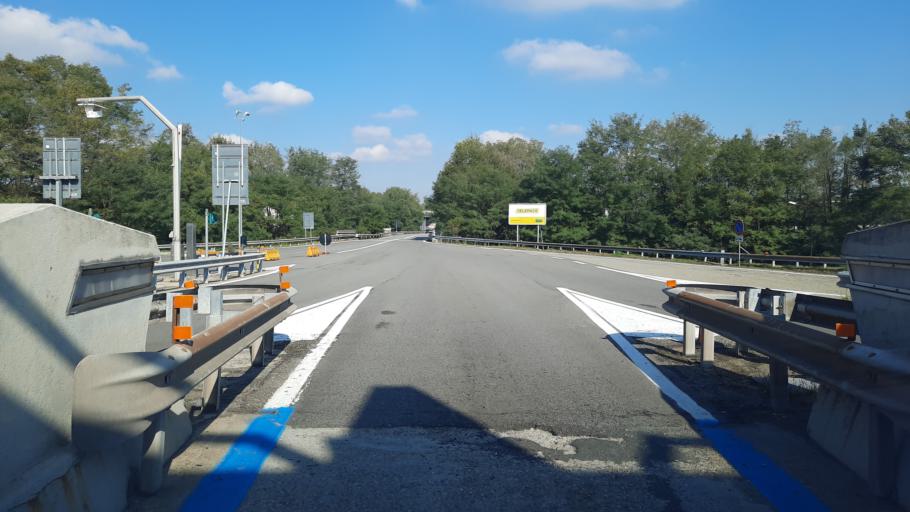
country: IT
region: Piedmont
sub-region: Provincia di Novara
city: Fontaneto D'Agogna
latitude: 45.6564
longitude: 8.4900
